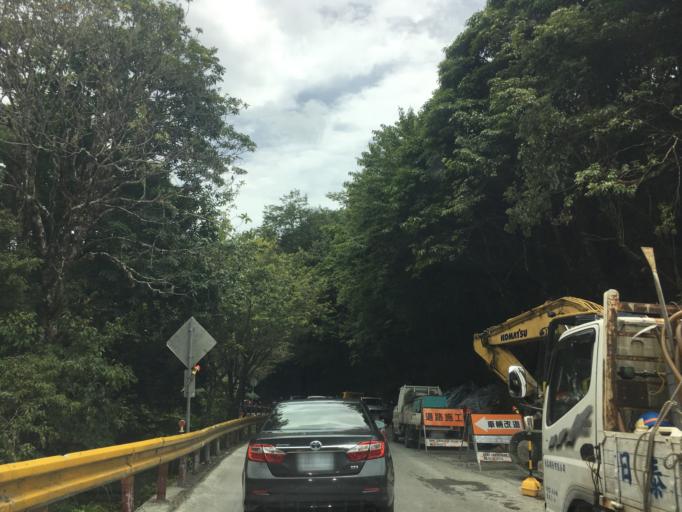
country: TW
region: Taiwan
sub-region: Hualien
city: Hualian
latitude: 24.1763
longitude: 121.3855
